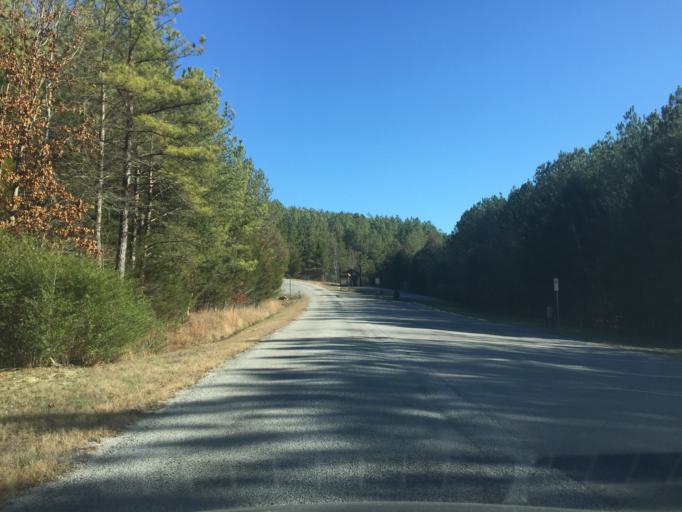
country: US
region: Tennessee
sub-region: Hamilton County
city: Harrison
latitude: 35.0910
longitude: -85.0973
